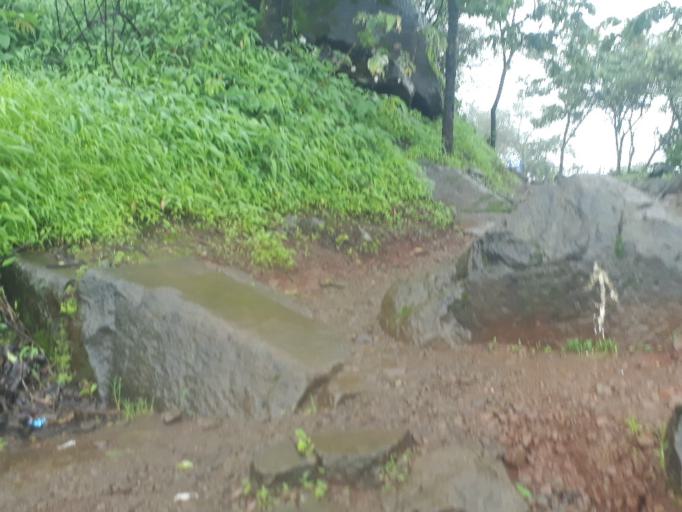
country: IN
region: Maharashtra
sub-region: Pune Division
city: Lonavla
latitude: 18.6319
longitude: 73.5150
